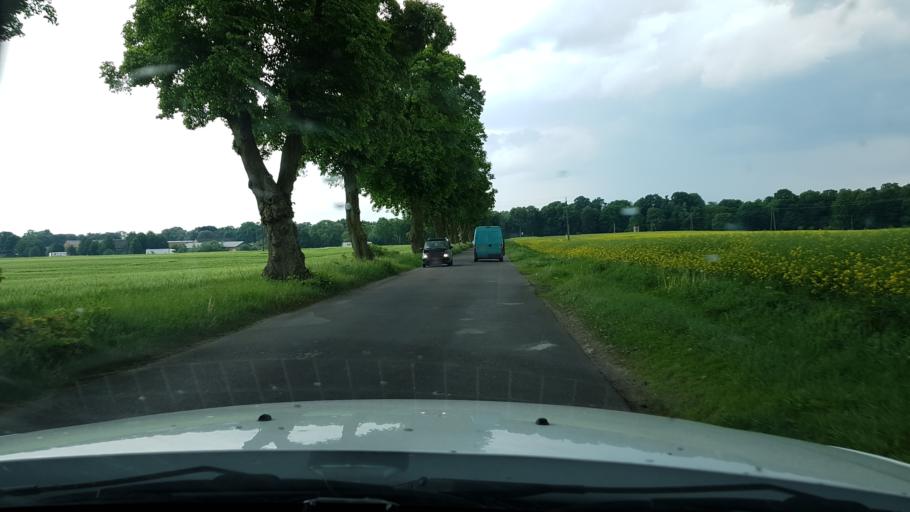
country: PL
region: West Pomeranian Voivodeship
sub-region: Powiat stargardzki
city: Dolice
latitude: 53.3052
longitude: 15.1748
